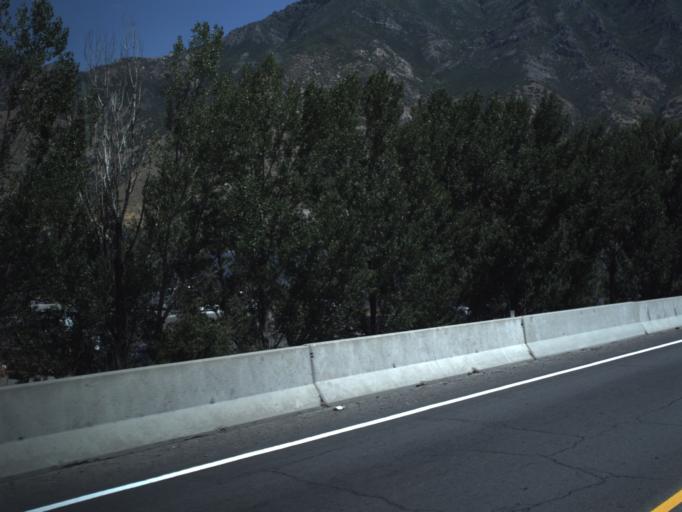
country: US
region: Utah
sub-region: Utah County
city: Springville
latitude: 40.1881
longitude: -111.6366
